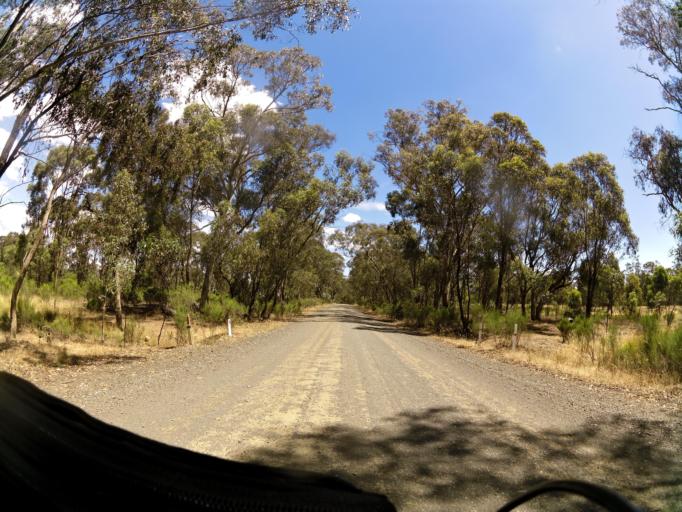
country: AU
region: Victoria
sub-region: Campaspe
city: Kyabram
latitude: -36.8017
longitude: 145.0766
